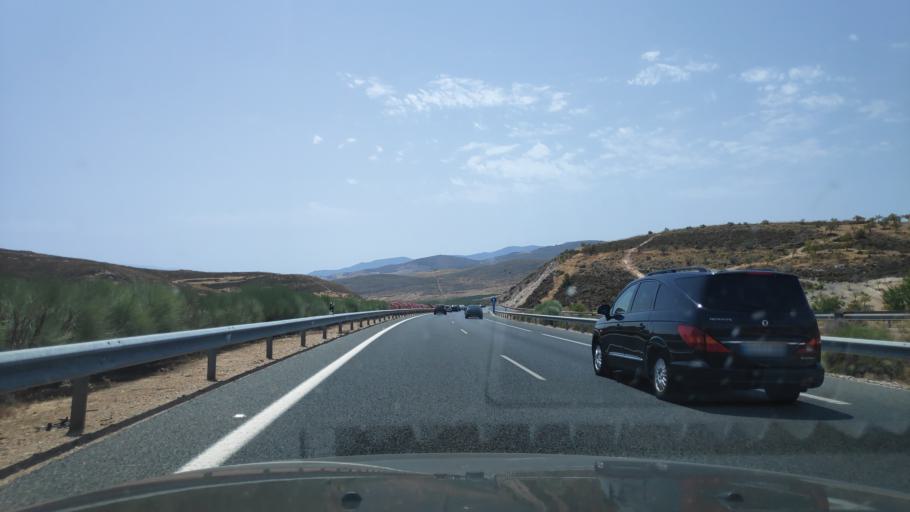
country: ES
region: Andalusia
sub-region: Provincia de Granada
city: Padul
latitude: 36.9990
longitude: -3.6304
